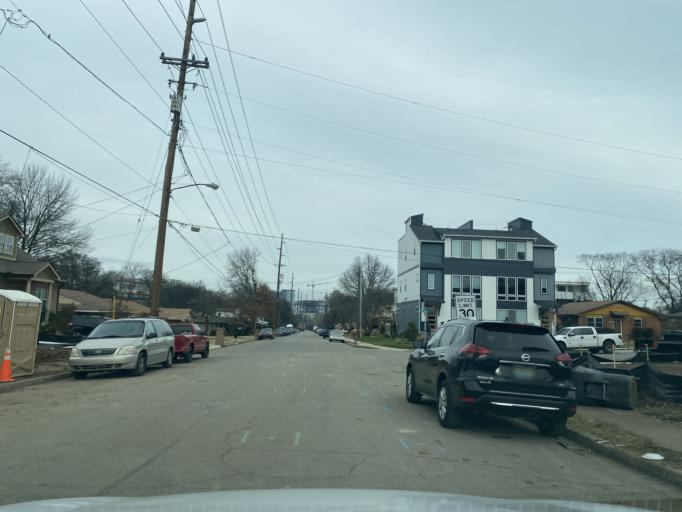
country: US
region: Tennessee
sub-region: Davidson County
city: Nashville
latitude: 36.1446
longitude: -86.7893
